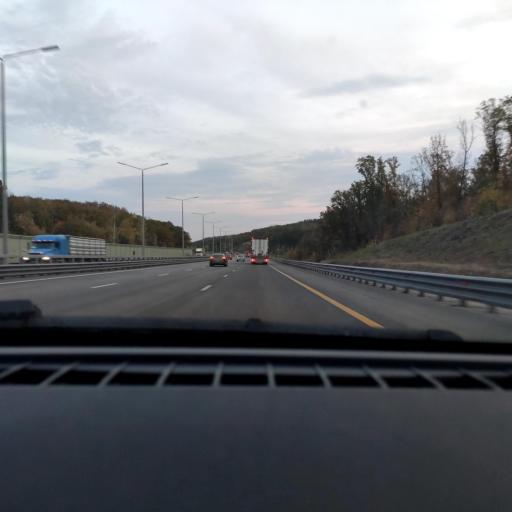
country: RU
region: Voronezj
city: Podgornoye
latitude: 51.8042
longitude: 39.2541
